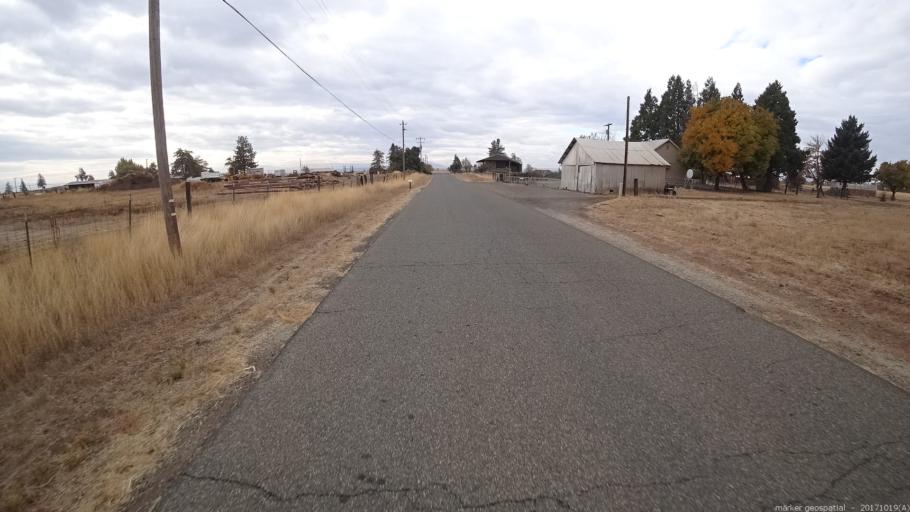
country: US
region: California
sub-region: Shasta County
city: Burney
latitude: 41.0571
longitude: -121.3891
